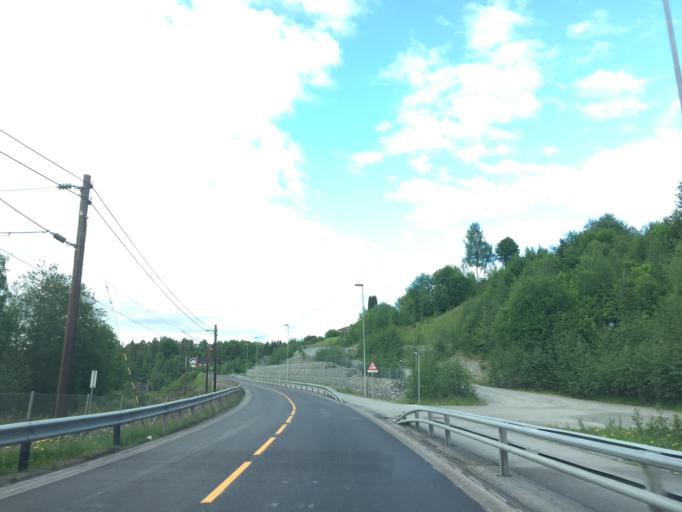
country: NO
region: Akershus
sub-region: Fet
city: Fetsund
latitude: 59.9293
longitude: 11.1785
